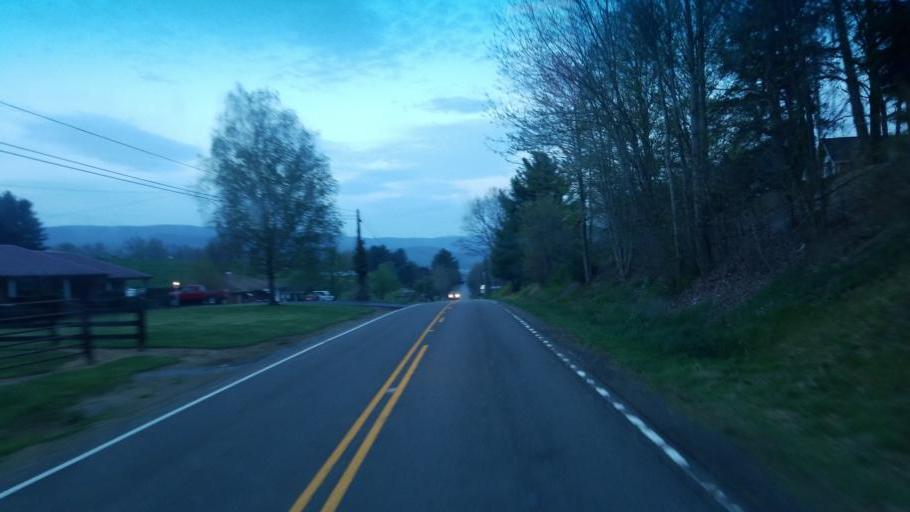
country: US
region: Virginia
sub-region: Smyth County
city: Atkins
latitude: 36.7903
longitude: -81.4017
